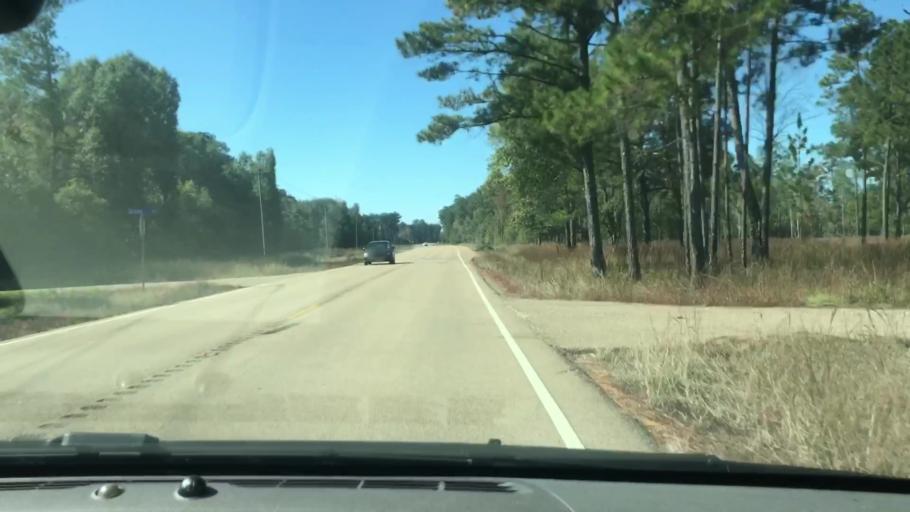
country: US
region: Louisiana
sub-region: Saint Tammany Parish
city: Abita Springs
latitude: 30.5058
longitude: -89.9659
